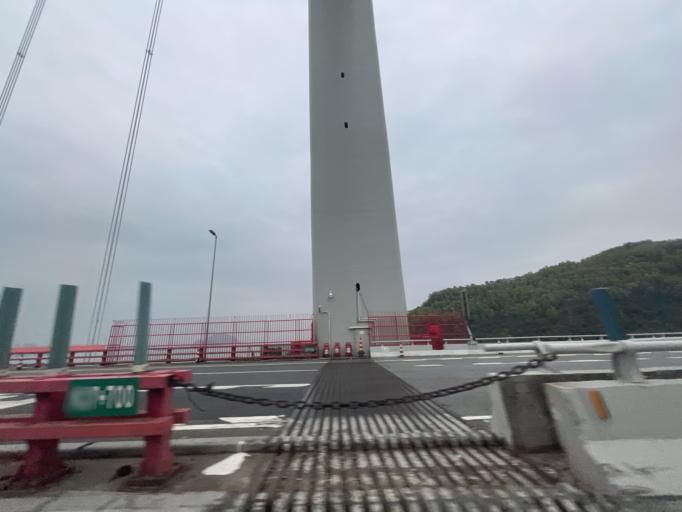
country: CN
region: Guangdong
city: Xinwan
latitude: 22.7993
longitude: 113.6192
